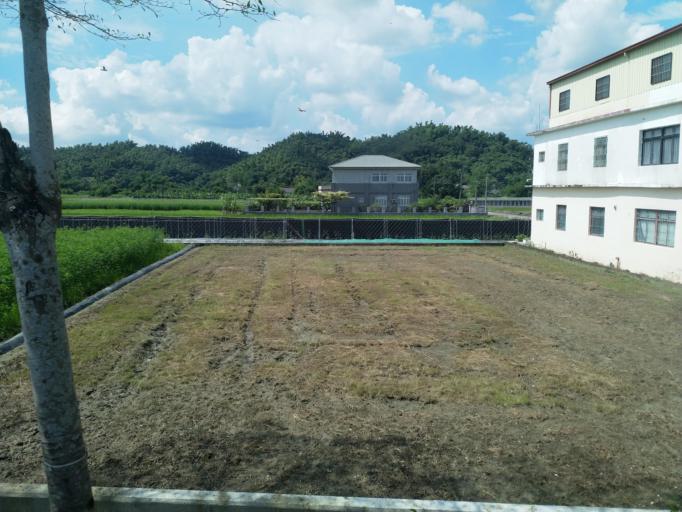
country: TW
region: Taiwan
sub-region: Pingtung
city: Pingtung
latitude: 22.8872
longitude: 120.5791
